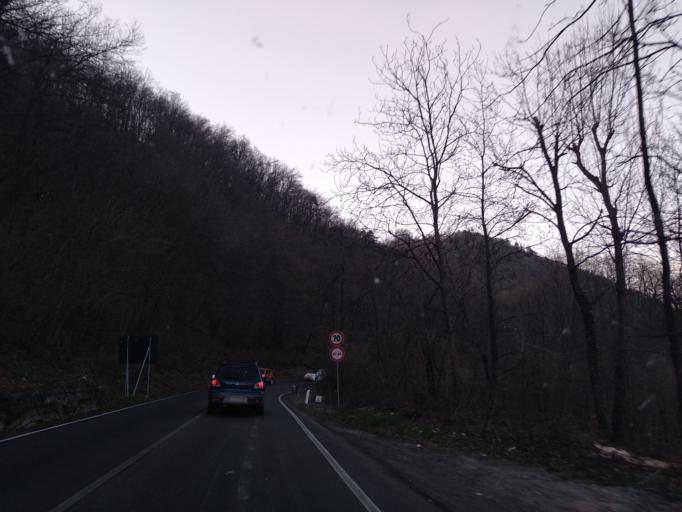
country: IT
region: Emilia-Romagna
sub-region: Provincia di Reggio Emilia
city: Casina
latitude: 44.5392
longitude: 10.5195
